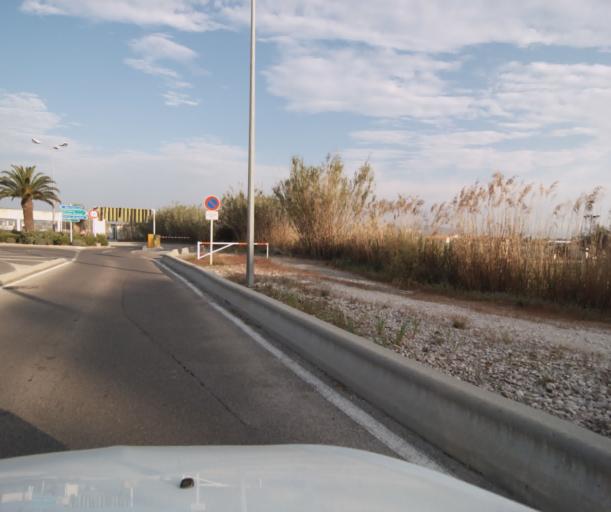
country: FR
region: Provence-Alpes-Cote d'Azur
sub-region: Departement du Var
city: Hyeres
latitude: 43.0943
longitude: 6.1600
